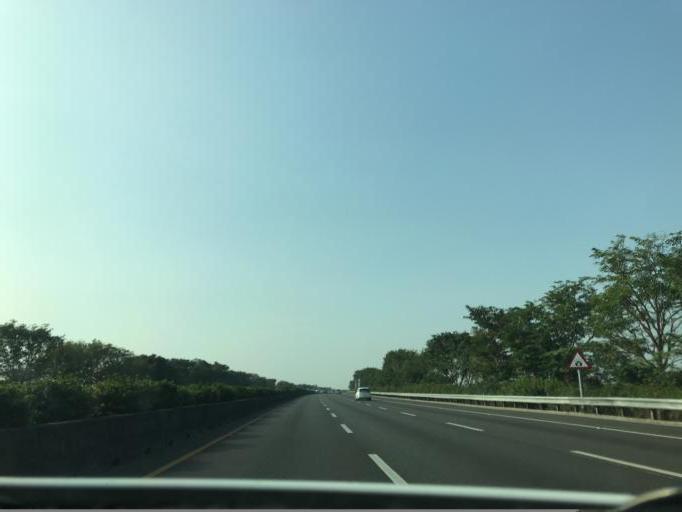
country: TW
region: Taiwan
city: Xinying
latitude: 23.3764
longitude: 120.3522
